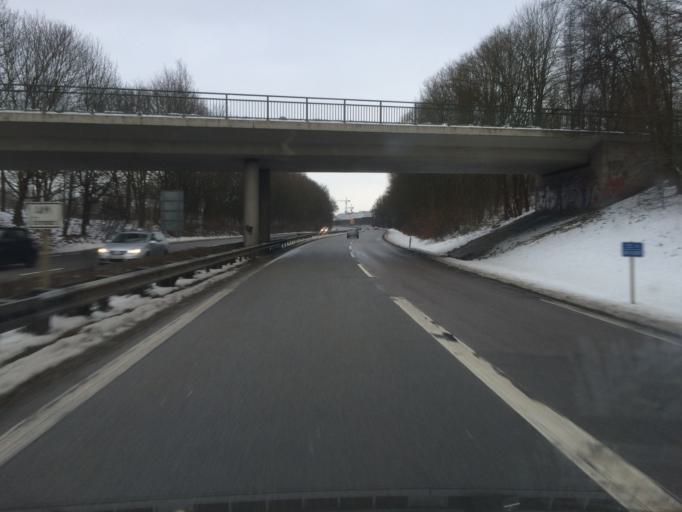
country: DE
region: Bavaria
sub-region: Upper Palatinate
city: Pentling
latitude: 49.0021
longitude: 12.0702
